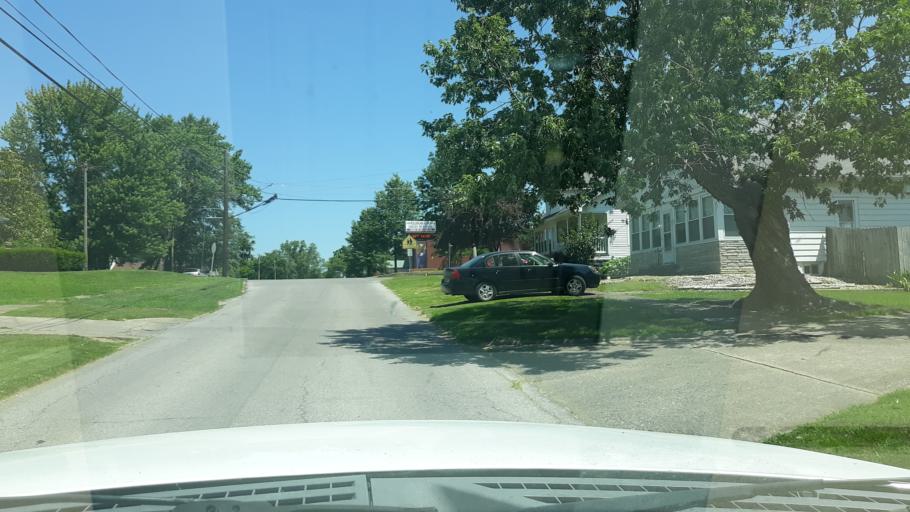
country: US
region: Illinois
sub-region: Saline County
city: Eldorado
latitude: 37.8192
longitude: -88.4361
